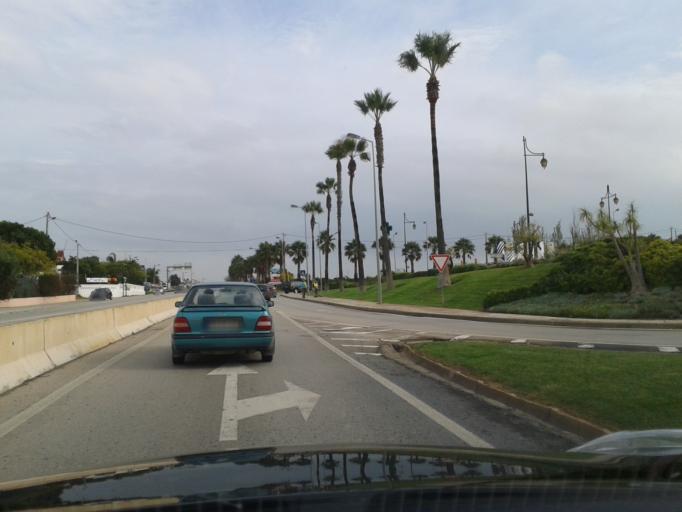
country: PT
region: Faro
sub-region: Albufeira
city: Guia
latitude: 37.1288
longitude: -8.2795
